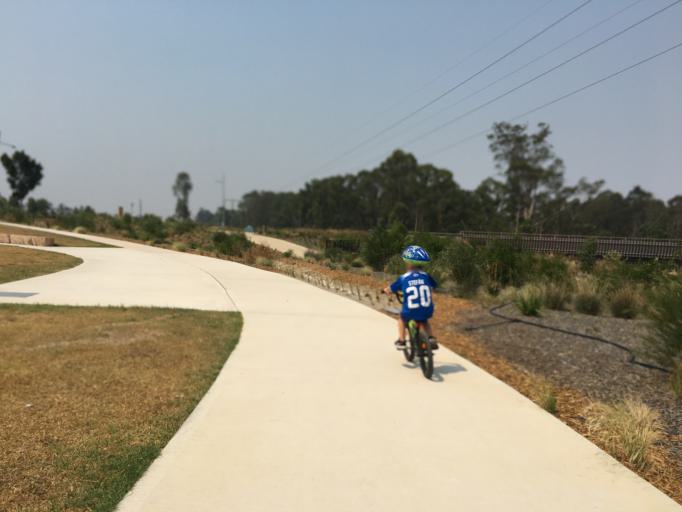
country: AU
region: New South Wales
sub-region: Campbelltown Municipality
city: Denham Court
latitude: -33.9789
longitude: 150.8122
